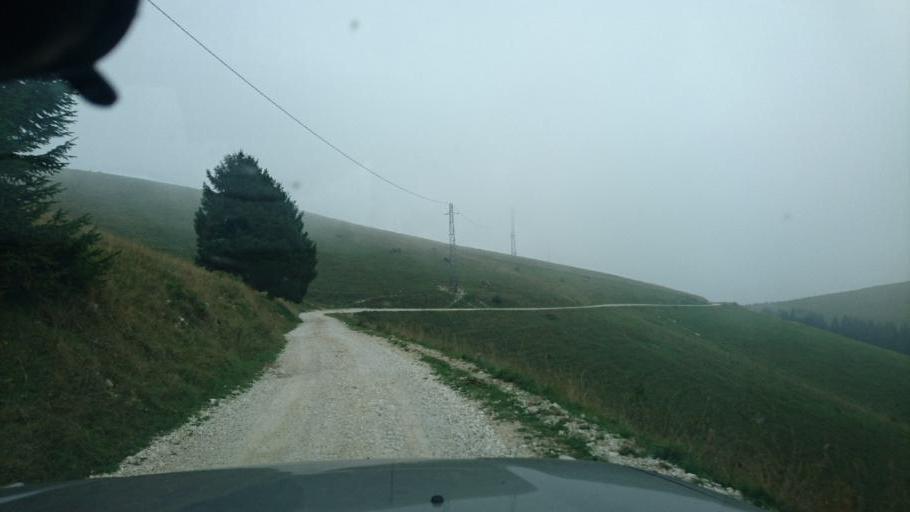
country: IT
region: Veneto
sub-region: Provincia di Vicenza
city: Enego
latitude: 45.9367
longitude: 11.6653
